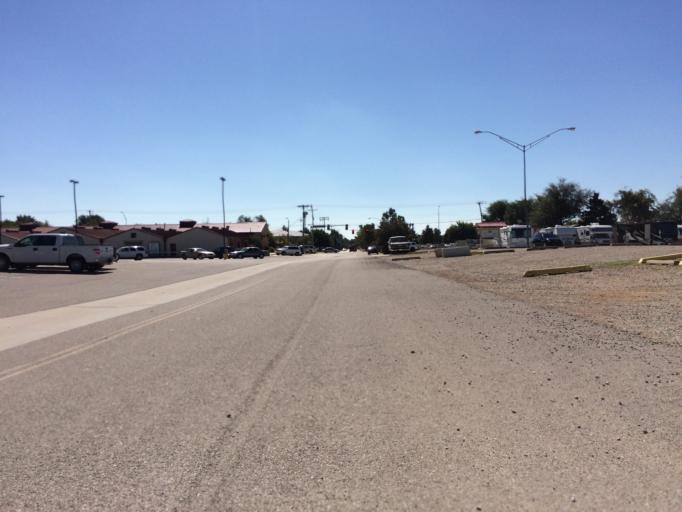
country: US
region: Oklahoma
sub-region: Cleveland County
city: Norman
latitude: 35.2343
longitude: -97.4375
